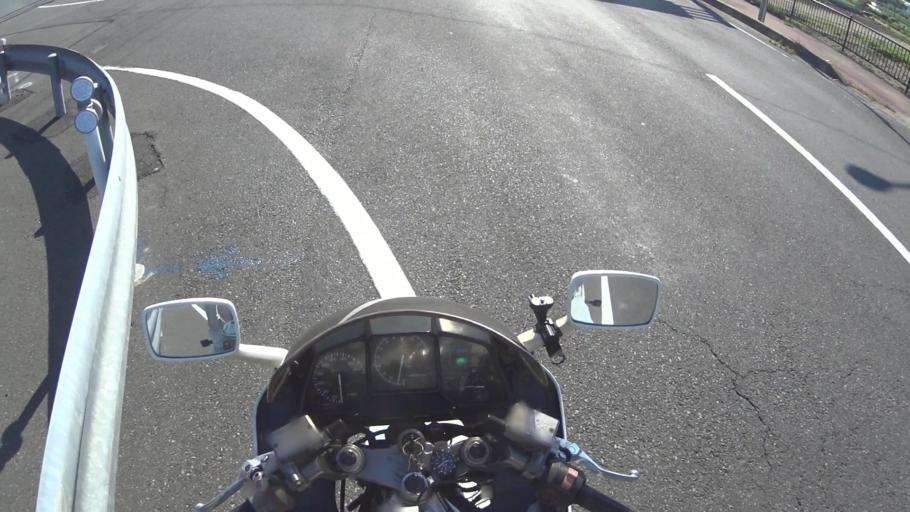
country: JP
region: Kyoto
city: Miyazu
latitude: 35.7403
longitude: 135.1098
